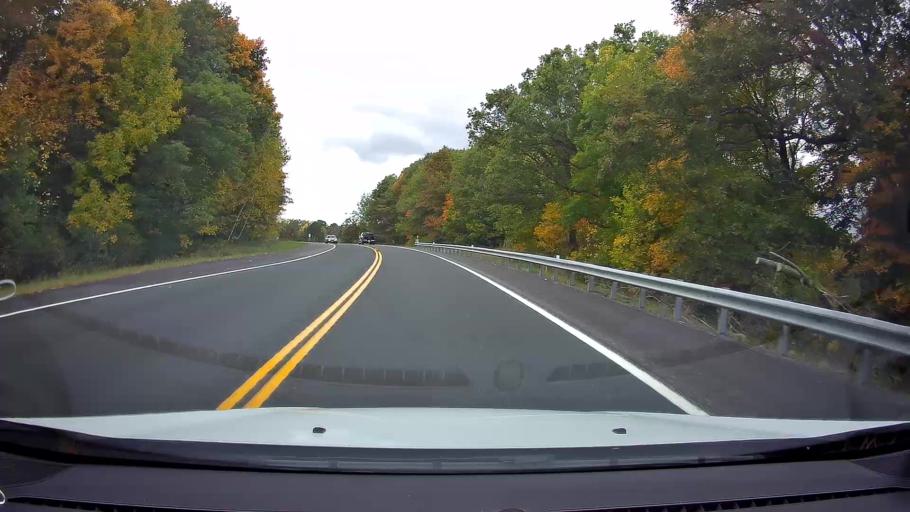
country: US
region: Wisconsin
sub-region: Polk County
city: Saint Croix Falls
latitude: 45.4186
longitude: -92.6560
